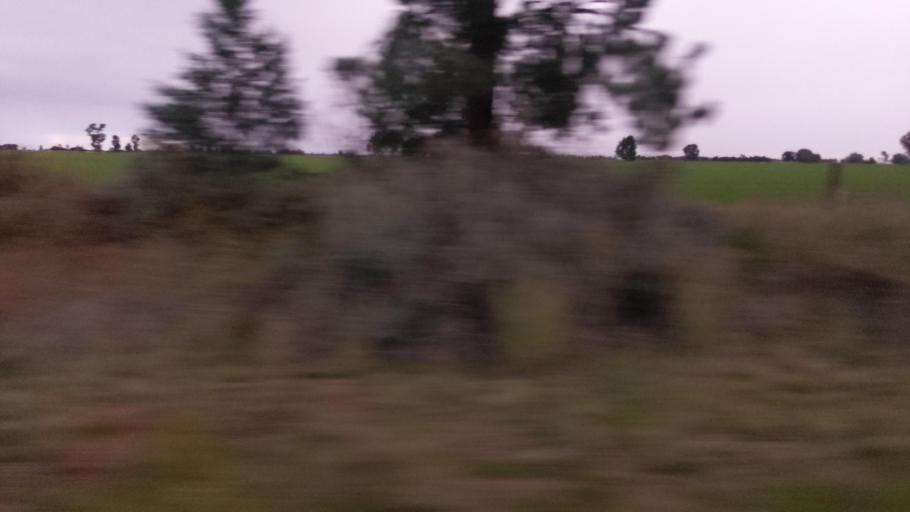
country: AU
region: New South Wales
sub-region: Narrandera
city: Narrandera
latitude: -34.7480
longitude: 146.8231
